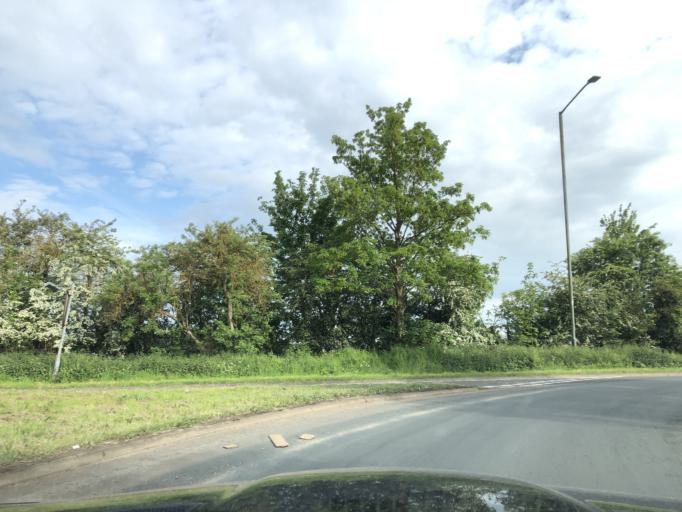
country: GB
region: England
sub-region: Warwickshire
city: Shipston on Stour
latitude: 52.1129
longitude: -1.6168
